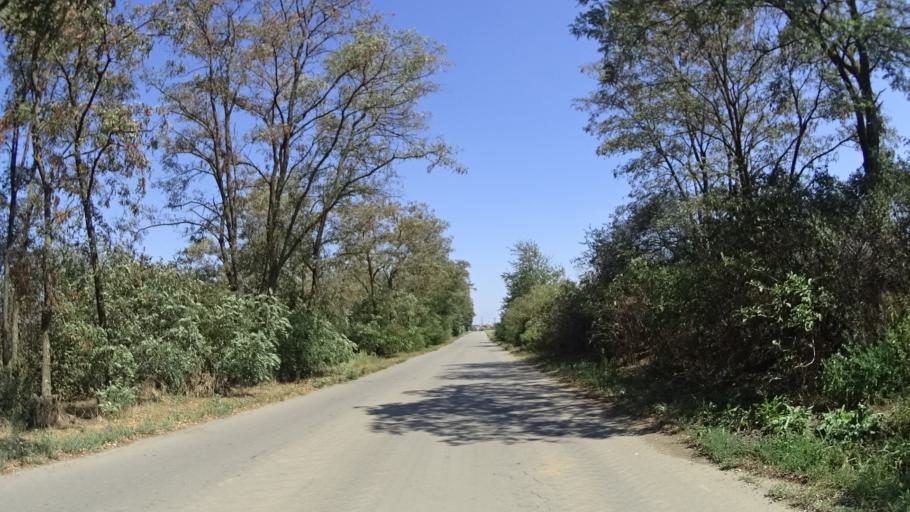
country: CZ
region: South Moravian
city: Petrov
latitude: 48.8880
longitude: 17.2925
